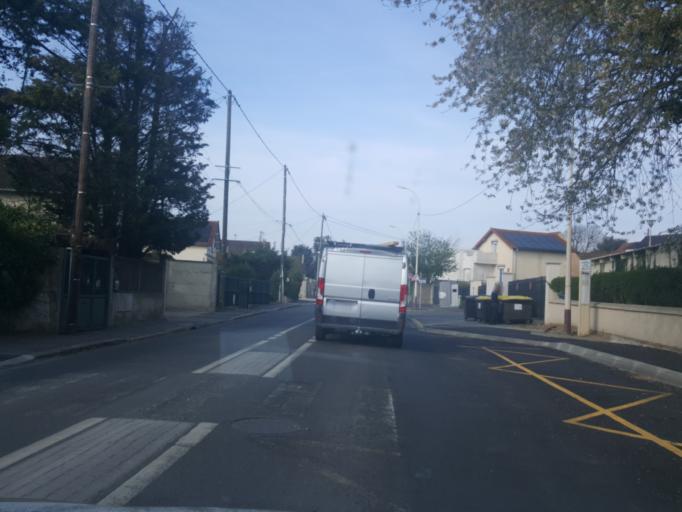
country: FR
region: Ile-de-France
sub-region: Departement de l'Essonne
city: Longpont-sur-Orge
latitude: 48.6460
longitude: 2.3013
